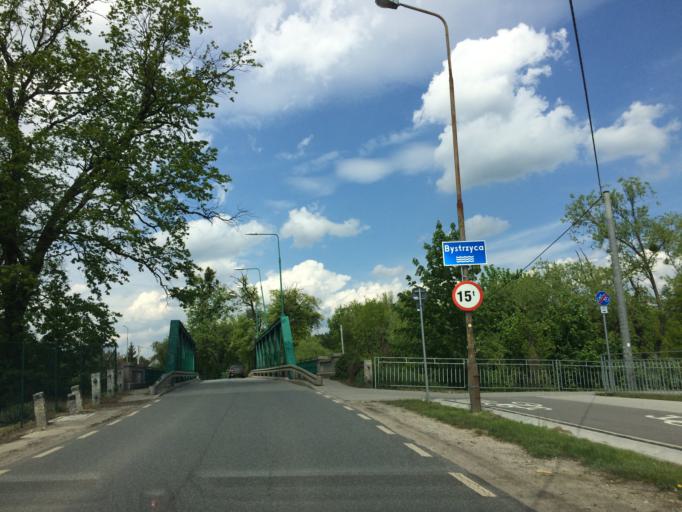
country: PL
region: Lower Silesian Voivodeship
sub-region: Powiat wroclawski
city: Smolec
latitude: 51.1664
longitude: 16.8922
